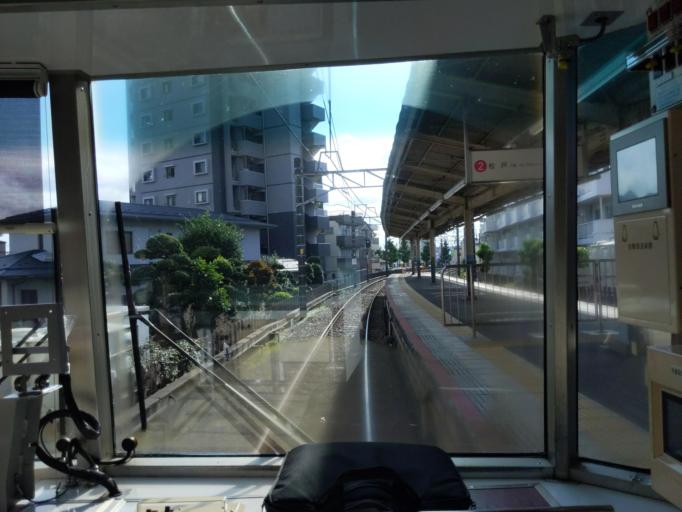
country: JP
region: Chiba
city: Matsudo
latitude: 35.7911
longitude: 139.9372
